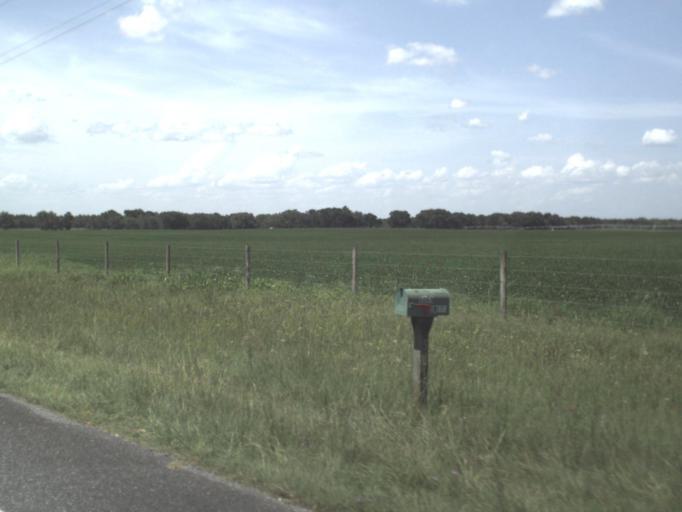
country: US
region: Florida
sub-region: Alachua County
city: High Springs
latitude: 29.8123
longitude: -82.7413
